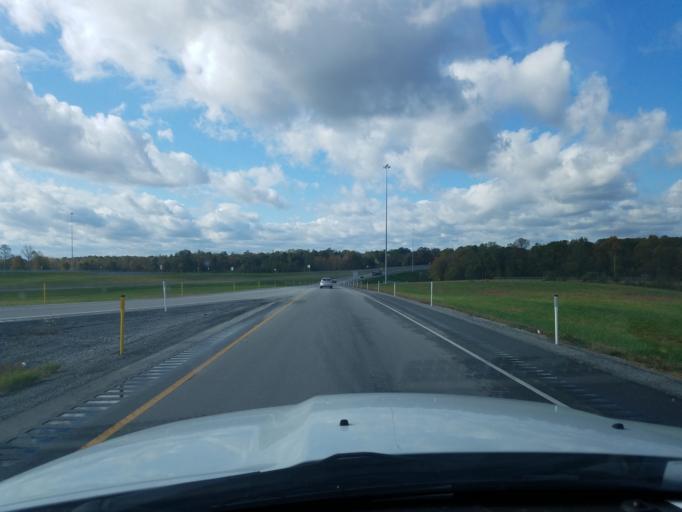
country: US
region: Kentucky
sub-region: Russell County
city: Russell Springs
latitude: 37.0532
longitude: -85.0705
